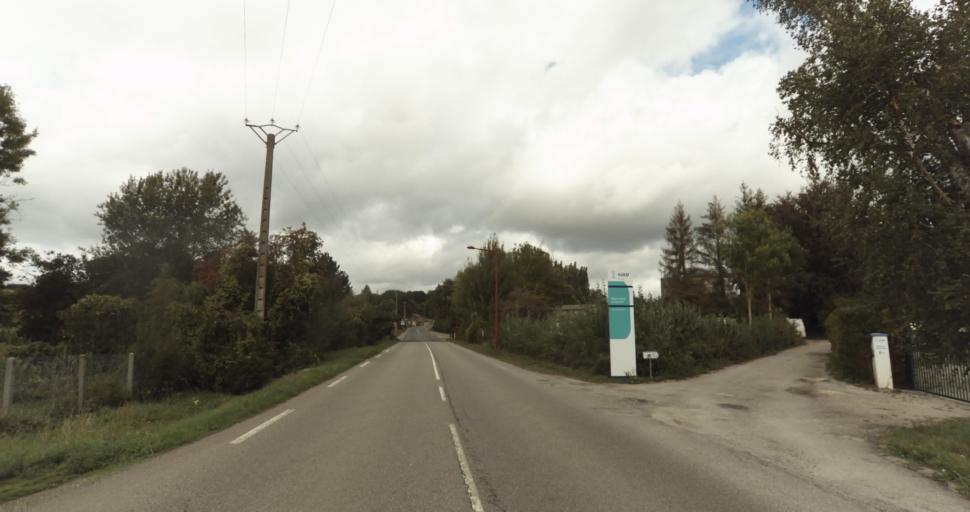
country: FR
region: Lower Normandy
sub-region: Departement de l'Orne
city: Gace
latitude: 48.7993
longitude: 0.2916
